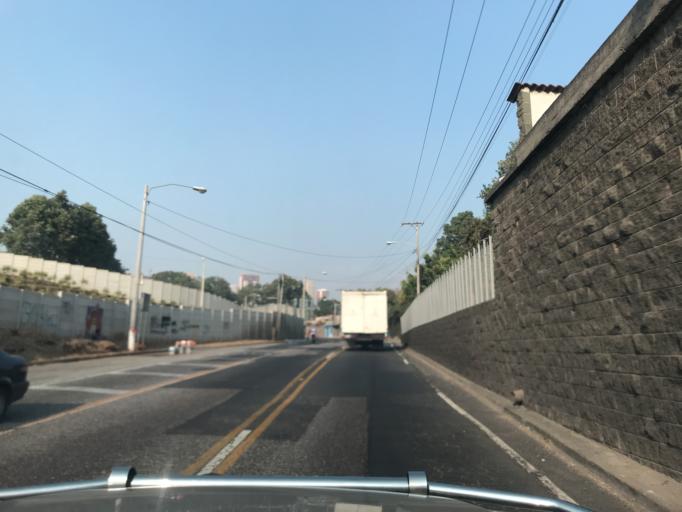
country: GT
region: Guatemala
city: Santa Catarina Pinula
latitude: 14.5611
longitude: -90.5291
